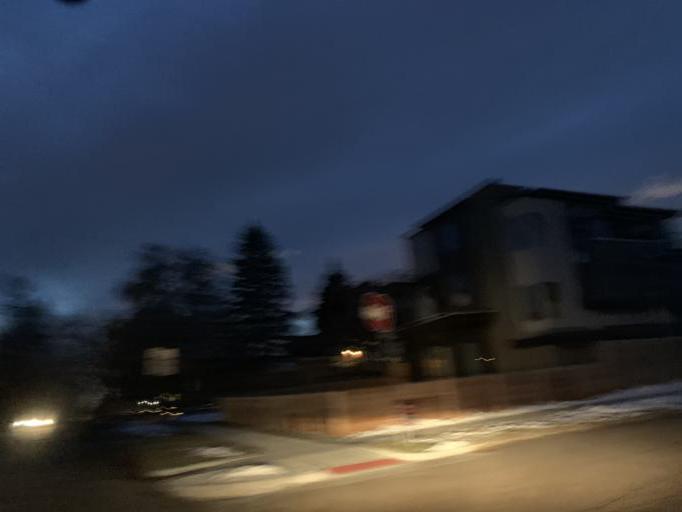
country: US
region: Colorado
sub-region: Jefferson County
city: Edgewater
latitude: 39.7748
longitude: -105.0452
